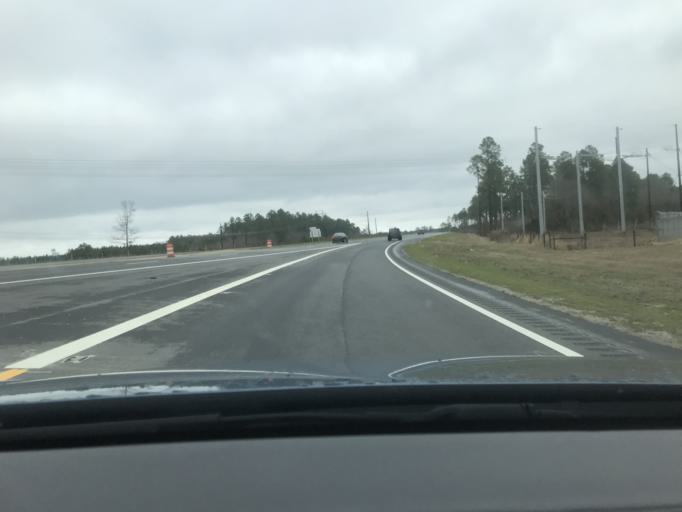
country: US
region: North Carolina
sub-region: Cumberland County
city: Fort Bragg
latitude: 35.0680
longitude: -79.0229
